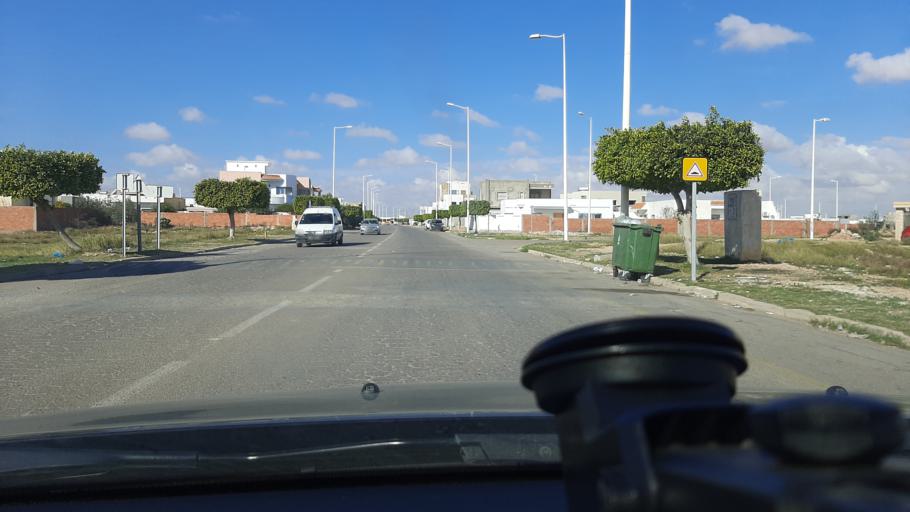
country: TN
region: Safaqis
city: Sfax
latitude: 34.8072
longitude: 10.7131
